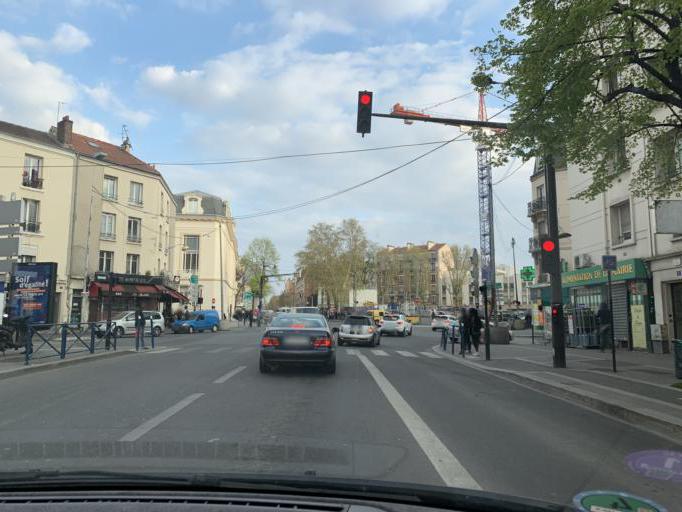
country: FR
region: Ile-de-France
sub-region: Departement de Seine-Saint-Denis
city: Aubervilliers
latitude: 48.9152
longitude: 2.3811
